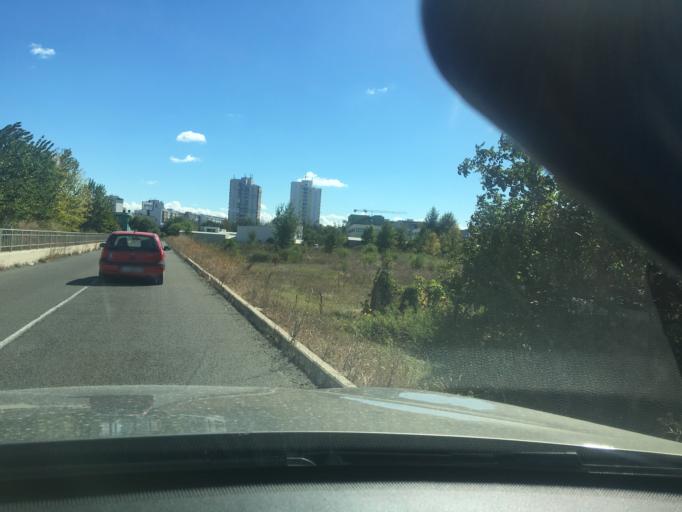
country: BG
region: Burgas
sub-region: Obshtina Burgas
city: Burgas
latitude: 42.5315
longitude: 27.4538
